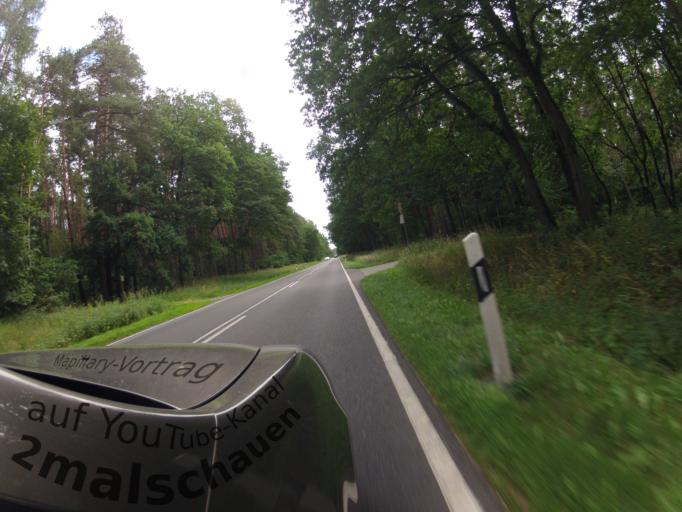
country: DE
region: Mecklenburg-Vorpommern
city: Lassan
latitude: 53.8917
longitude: 13.7885
